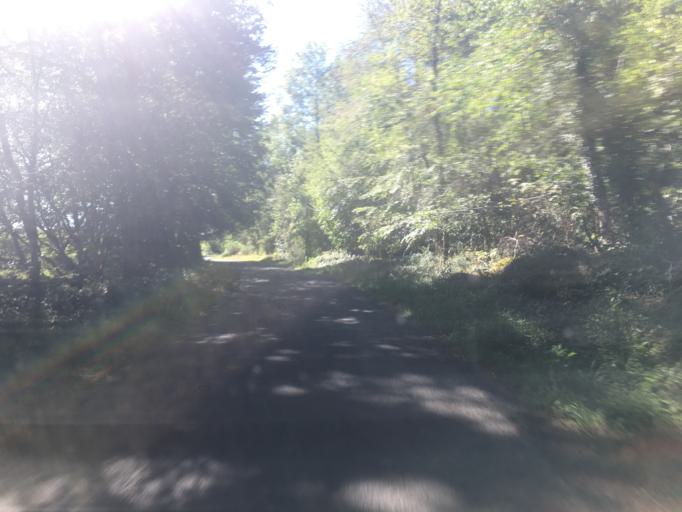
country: FR
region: Limousin
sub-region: Departement de la Correze
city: Bort-les-Orgues
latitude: 45.4079
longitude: 2.4866
